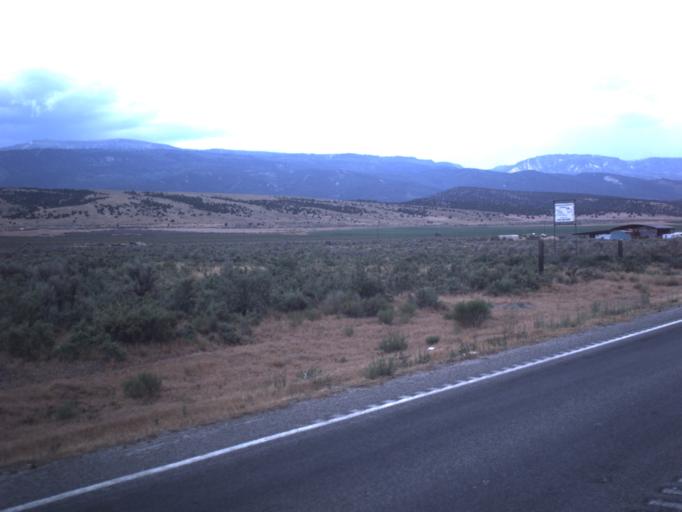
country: US
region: Utah
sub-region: Sanpete County
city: Moroni
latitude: 39.4472
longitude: -111.5625
